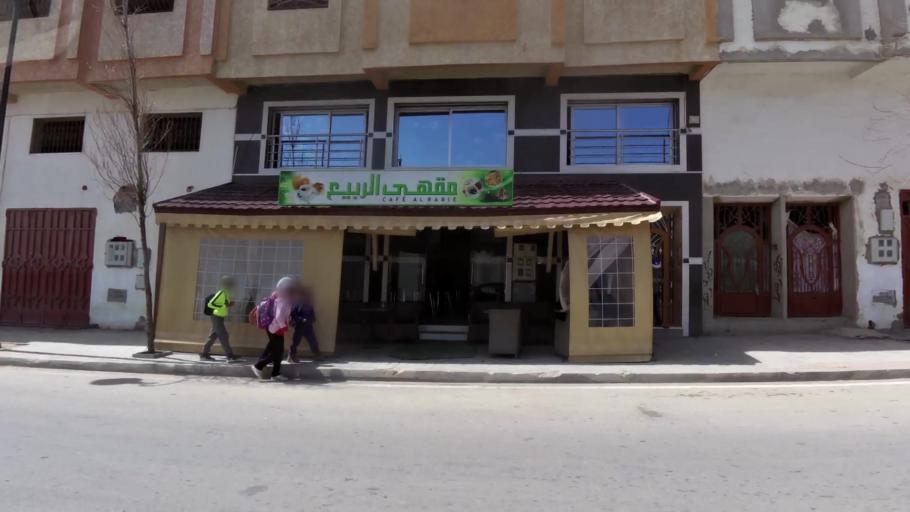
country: MA
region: Tanger-Tetouan
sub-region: Tanger-Assilah
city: Tangier
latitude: 35.7369
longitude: -5.8222
